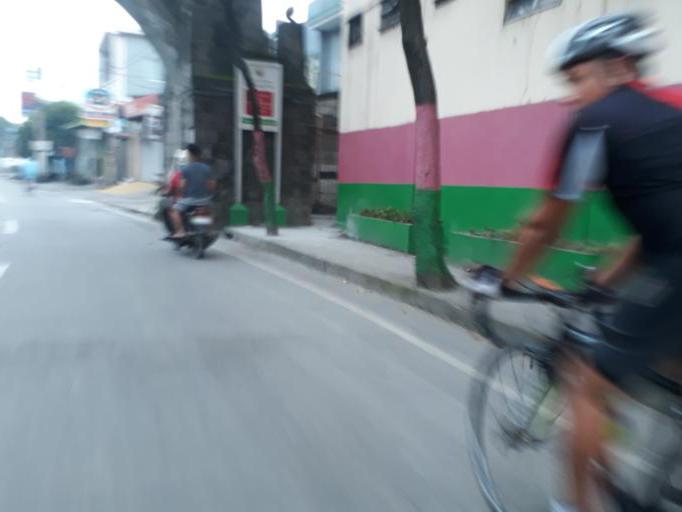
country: PH
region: Calabarzon
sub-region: Province of Rizal
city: Valenzuela
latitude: 14.6950
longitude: 120.9544
